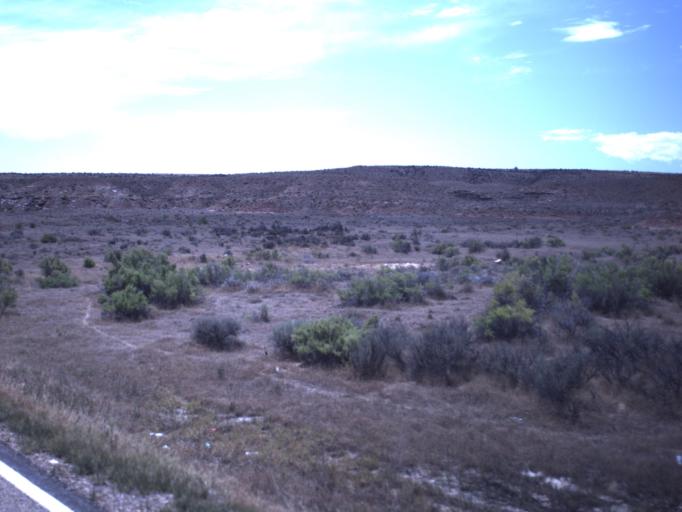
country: US
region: Utah
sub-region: Uintah County
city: Maeser
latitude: 40.3160
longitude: -109.6927
